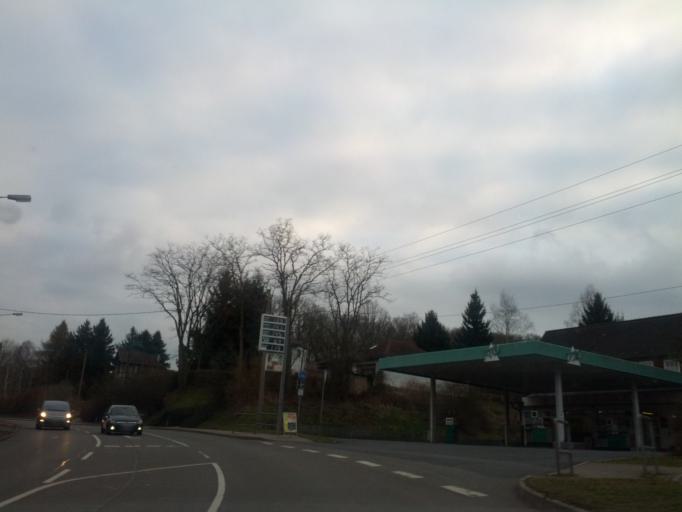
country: DE
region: Thuringia
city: Thal
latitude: 50.9355
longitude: 10.3904
